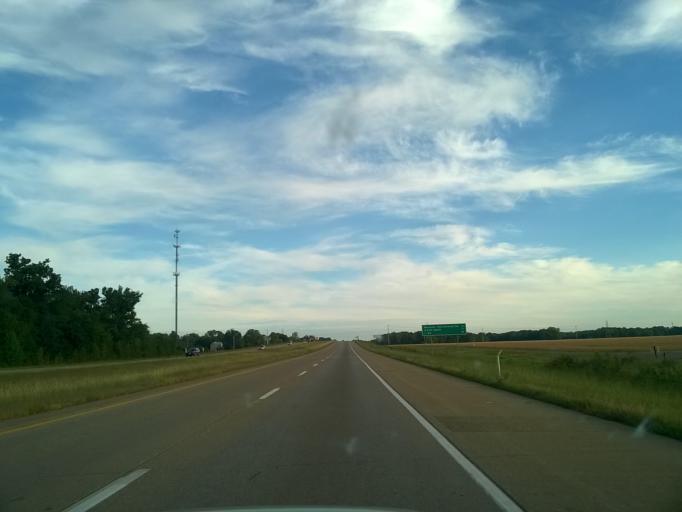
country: US
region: Indiana
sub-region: Vanderburgh County
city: Melody Hill
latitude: 38.0243
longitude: -87.4712
